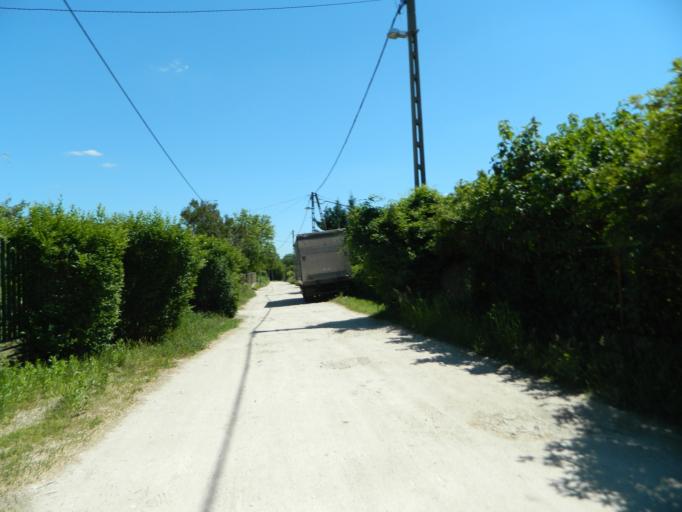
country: HU
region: Pest
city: Budakalasz
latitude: 47.6099
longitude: 19.0442
